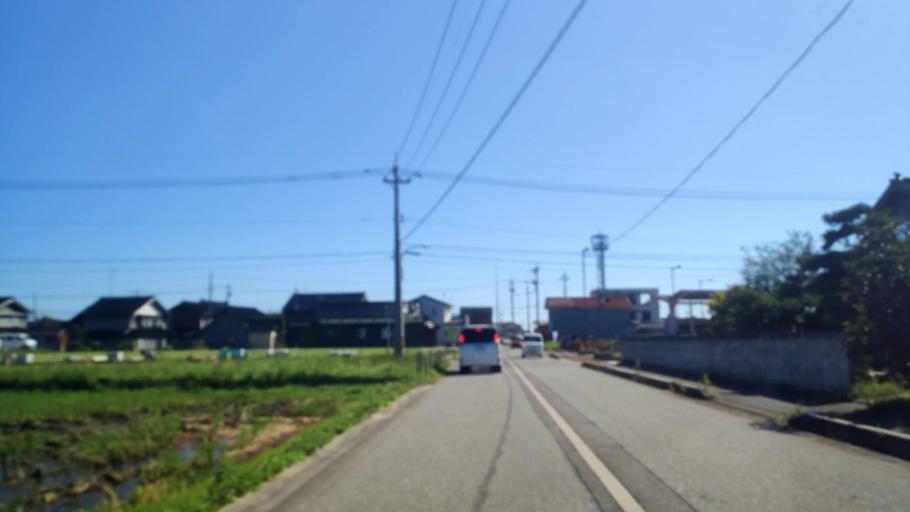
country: JP
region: Ishikawa
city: Nanao
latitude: 37.4422
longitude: 137.2706
